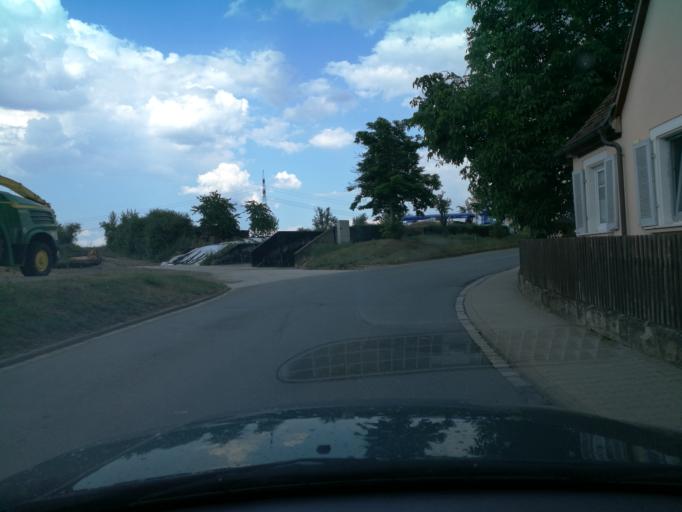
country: DE
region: Bavaria
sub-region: Regierungsbezirk Mittelfranken
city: Cadolzburg
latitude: 49.4719
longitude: 10.8265
